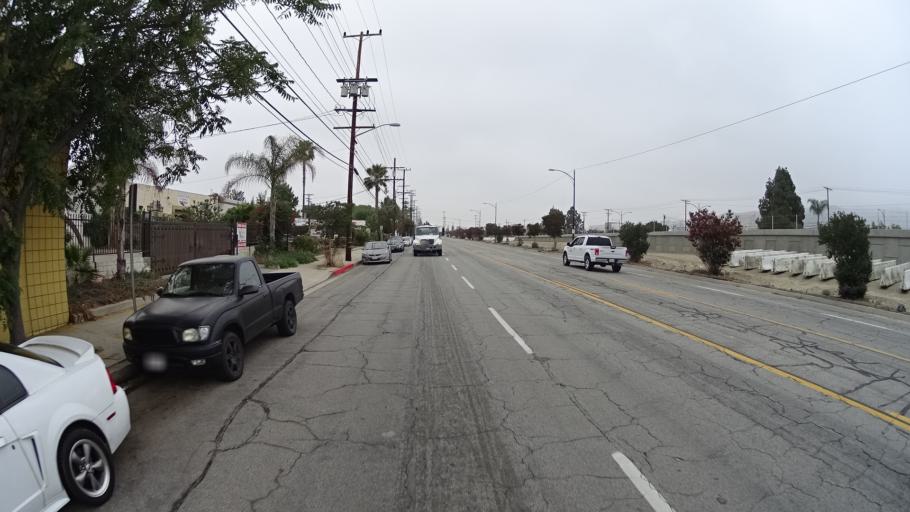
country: US
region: California
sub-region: Los Angeles County
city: Burbank
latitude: 34.2003
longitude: -118.3416
